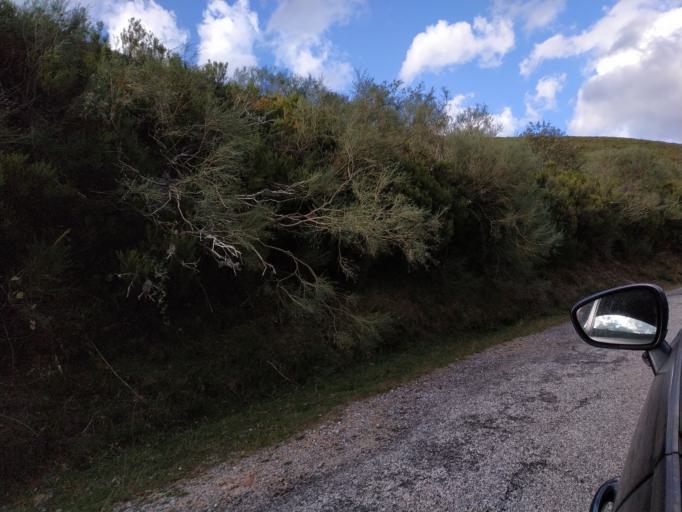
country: ES
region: Castille and Leon
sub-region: Provincia de Leon
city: Candin
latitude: 42.8718
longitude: -6.8349
